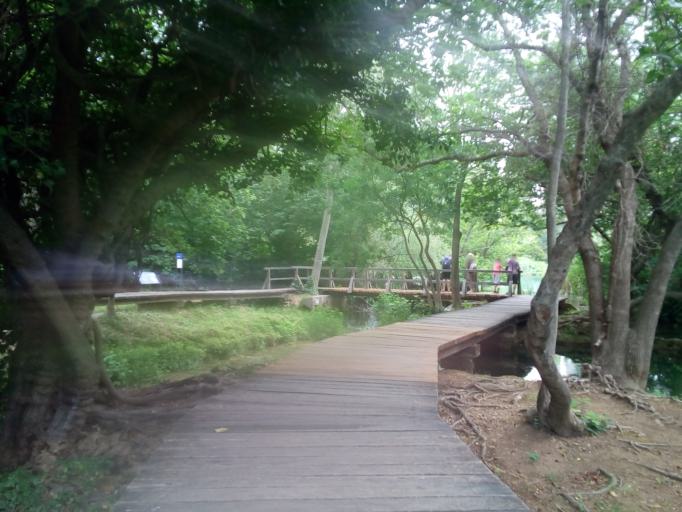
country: HR
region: Sibensko-Kniniska
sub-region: Grad Sibenik
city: Sibenik
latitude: 43.8038
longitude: 15.9666
